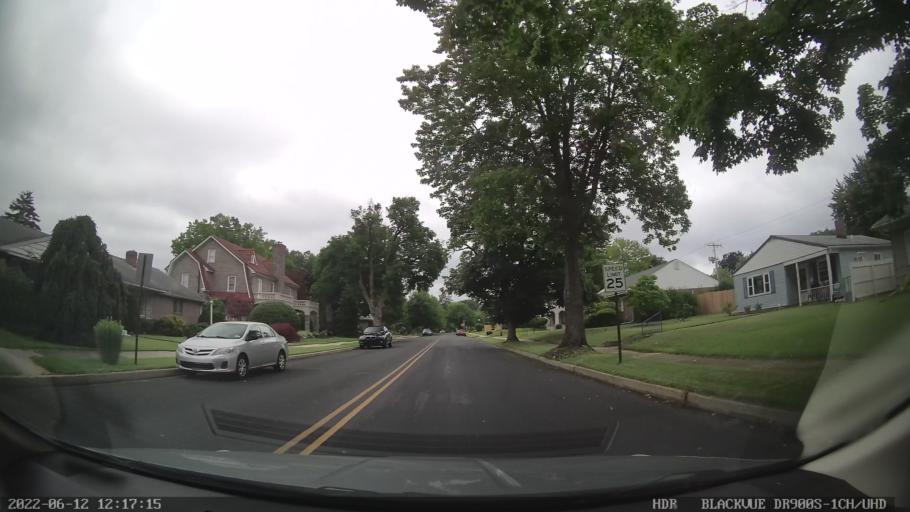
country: US
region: Pennsylvania
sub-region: Lehigh County
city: Dorneyville
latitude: 40.5892
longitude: -75.5086
